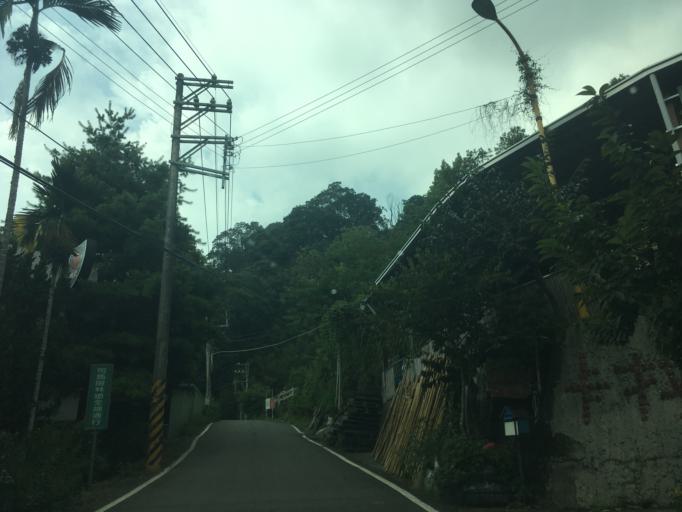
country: TW
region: Taiwan
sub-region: Miaoli
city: Miaoli
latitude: 24.3929
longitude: 120.9791
